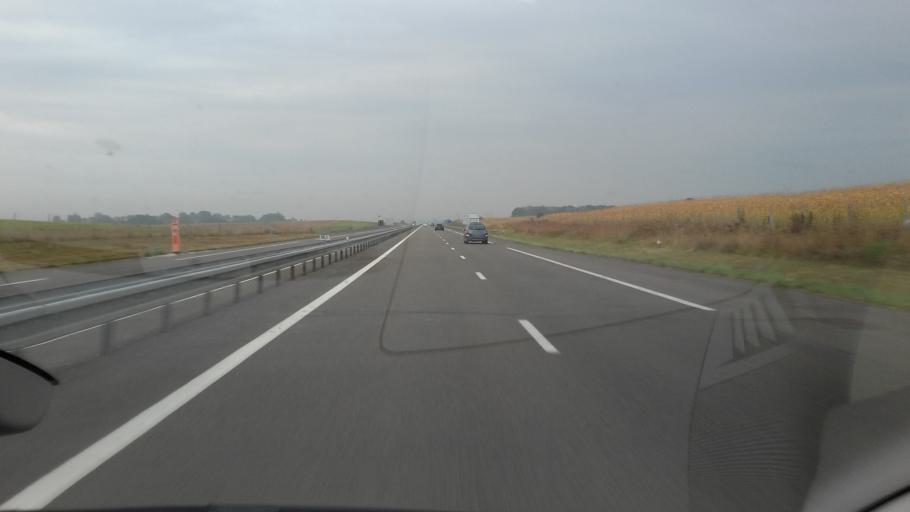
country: FR
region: Champagne-Ardenne
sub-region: Departement des Ardennes
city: Attigny
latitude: 49.5893
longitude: 4.4931
